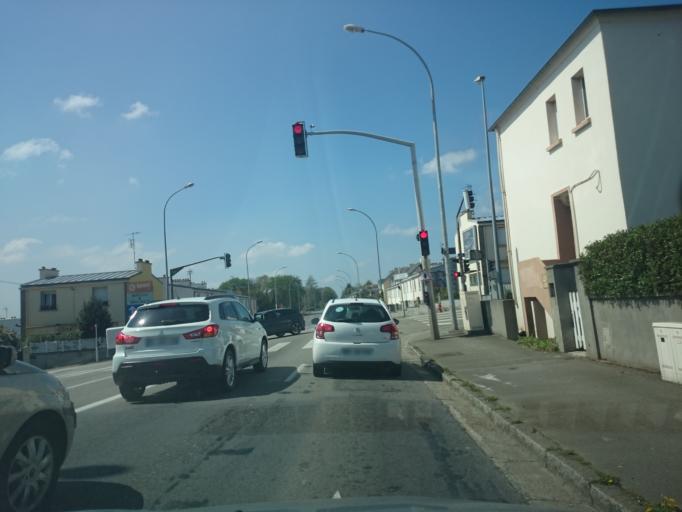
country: FR
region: Brittany
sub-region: Departement du Finistere
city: Brest
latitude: 48.4133
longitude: -4.4862
